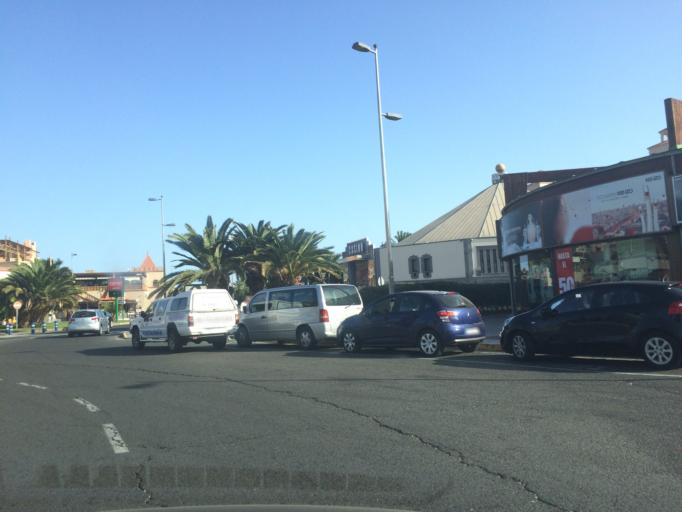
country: ES
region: Canary Islands
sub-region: Provincia de Las Palmas
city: Maspalomas
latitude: 27.7396
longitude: -15.6013
